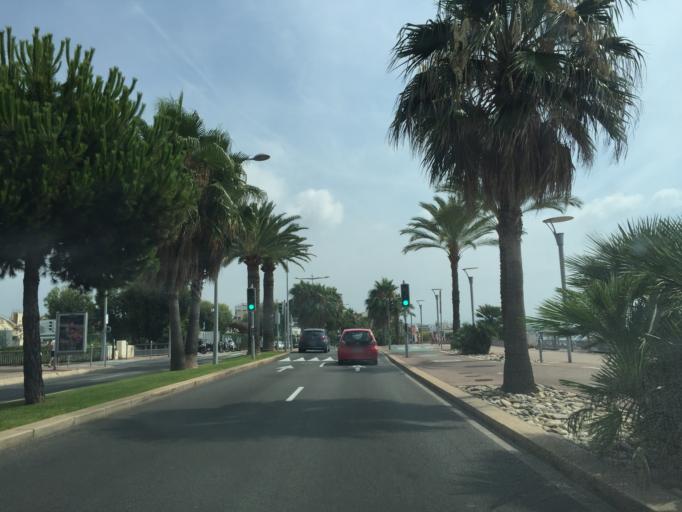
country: FR
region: Provence-Alpes-Cote d'Azur
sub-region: Departement des Alpes-Maritimes
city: Cagnes-sur-Mer
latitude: 43.6524
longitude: 7.1546
